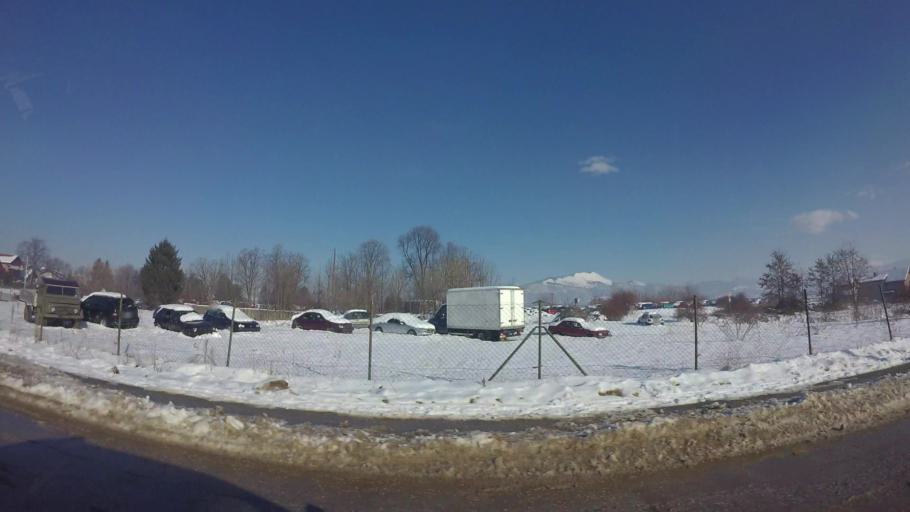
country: BA
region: Federation of Bosnia and Herzegovina
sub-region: Kanton Sarajevo
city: Sarajevo
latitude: 43.8113
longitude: 18.3271
